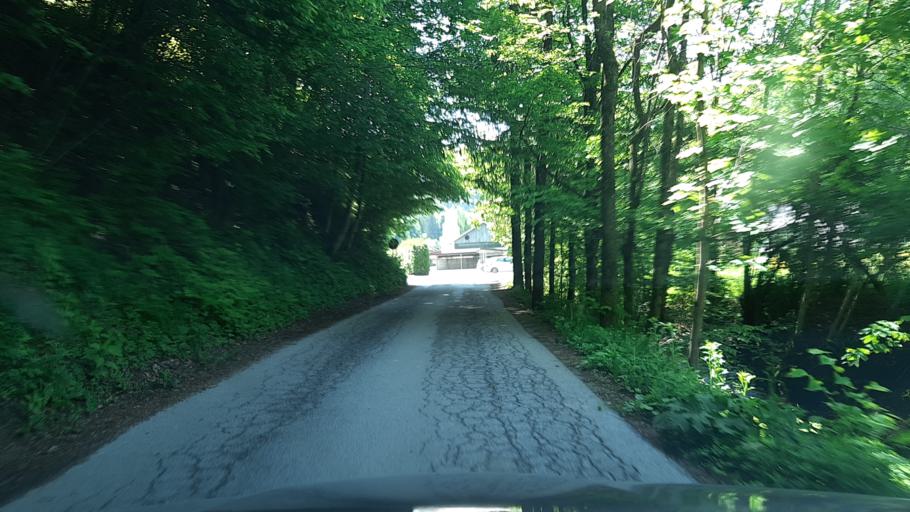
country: SI
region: Skofja Loka
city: Skofja Loka
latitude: 46.1486
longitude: 14.2941
